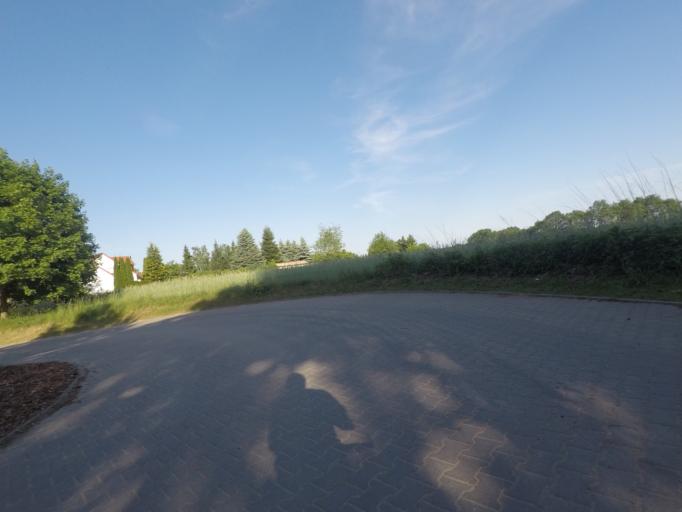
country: DE
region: Brandenburg
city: Joachimsthal
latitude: 52.8884
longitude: 13.6989
